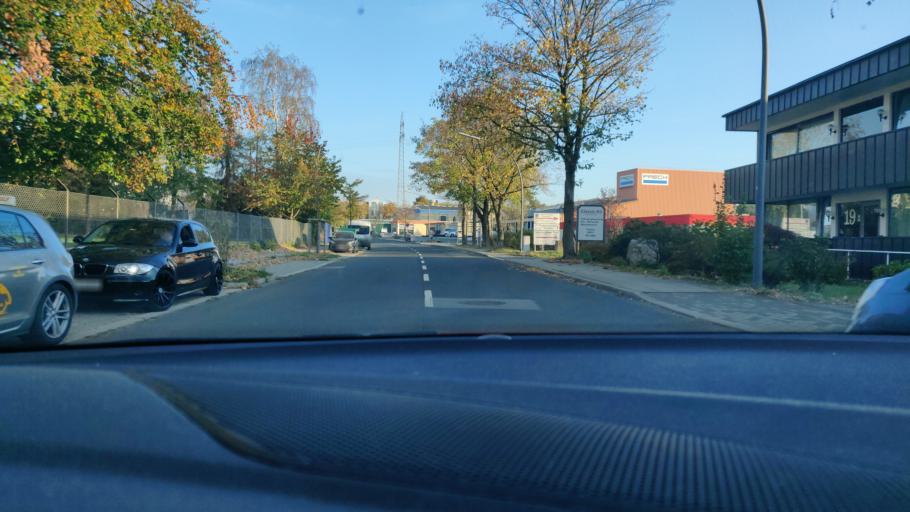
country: DE
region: North Rhine-Westphalia
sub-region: Regierungsbezirk Dusseldorf
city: Velbert
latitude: 51.3474
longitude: 7.0649
